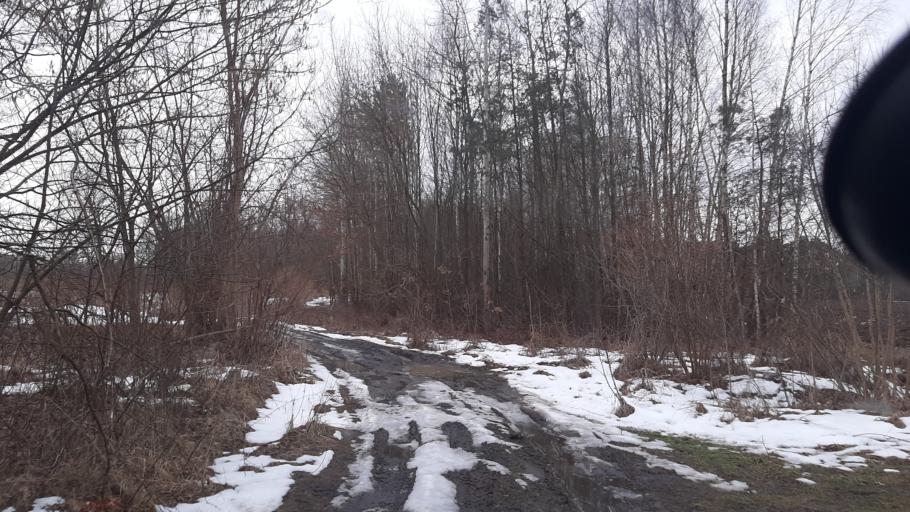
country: PL
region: Lublin Voivodeship
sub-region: Powiat wlodawski
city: Wlodawa
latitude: 51.5103
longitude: 23.6166
